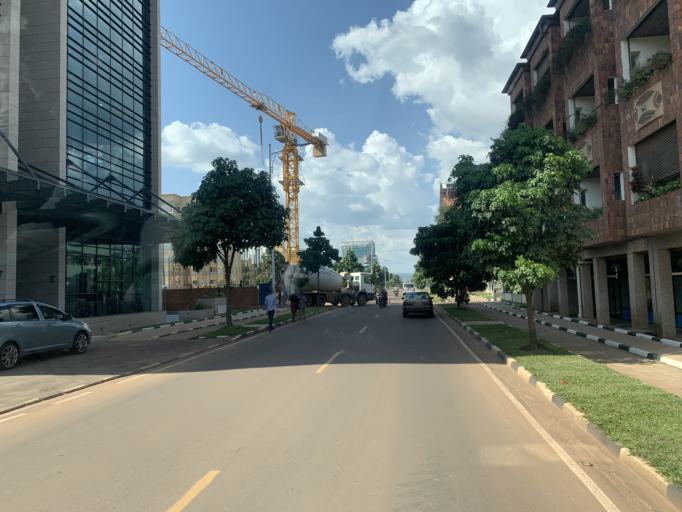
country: RW
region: Kigali
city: Kigali
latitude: -1.9518
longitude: 30.0615
